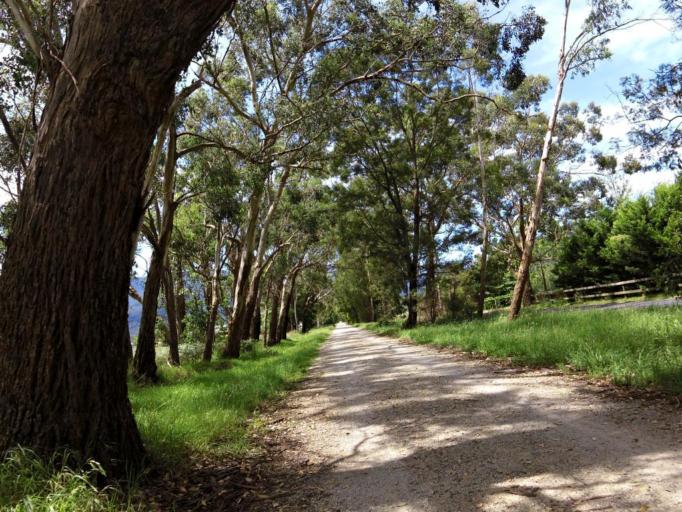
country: AU
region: Victoria
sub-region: Yarra Ranges
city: Yarra Junction
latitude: -37.7729
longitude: 145.6276
